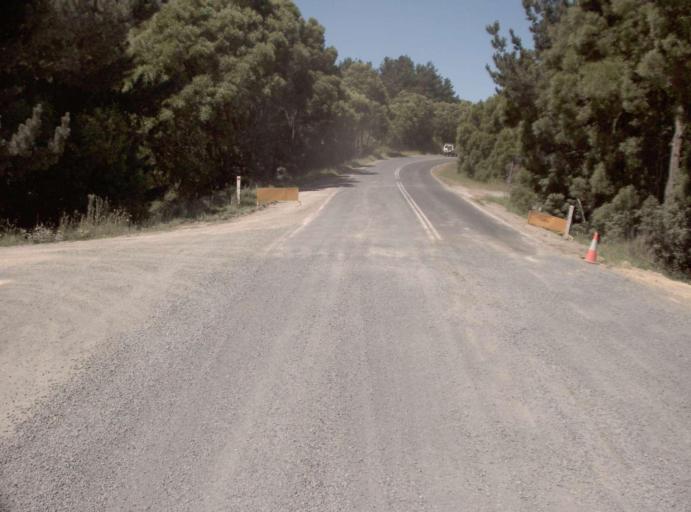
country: AU
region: Victoria
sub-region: Bass Coast
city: North Wonthaggi
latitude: -38.6955
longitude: 146.1046
